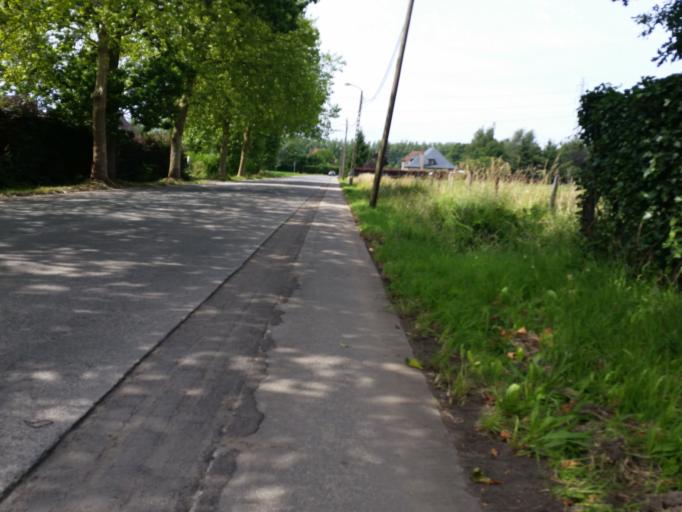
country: BE
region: Flanders
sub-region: Provincie Antwerpen
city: Rumst
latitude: 51.0540
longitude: 4.4123
